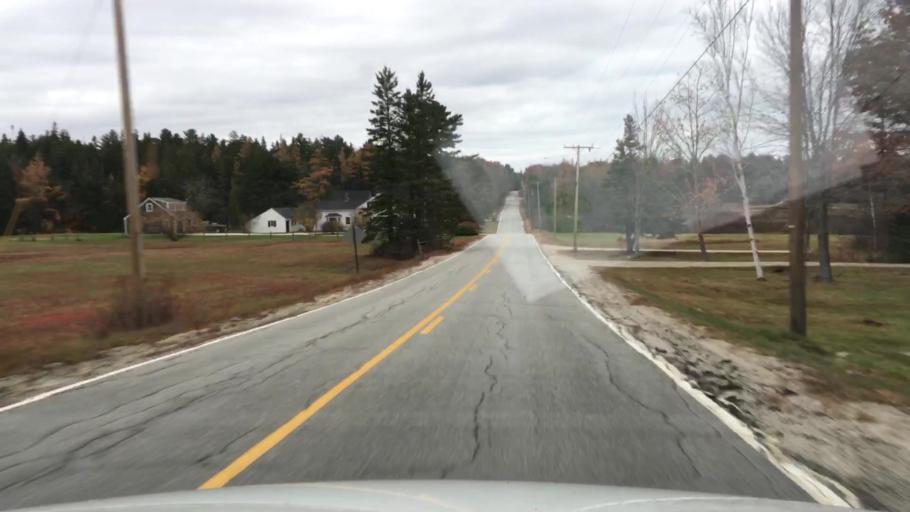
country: US
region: Maine
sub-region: Hancock County
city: Sedgwick
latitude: 44.3274
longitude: -68.5698
